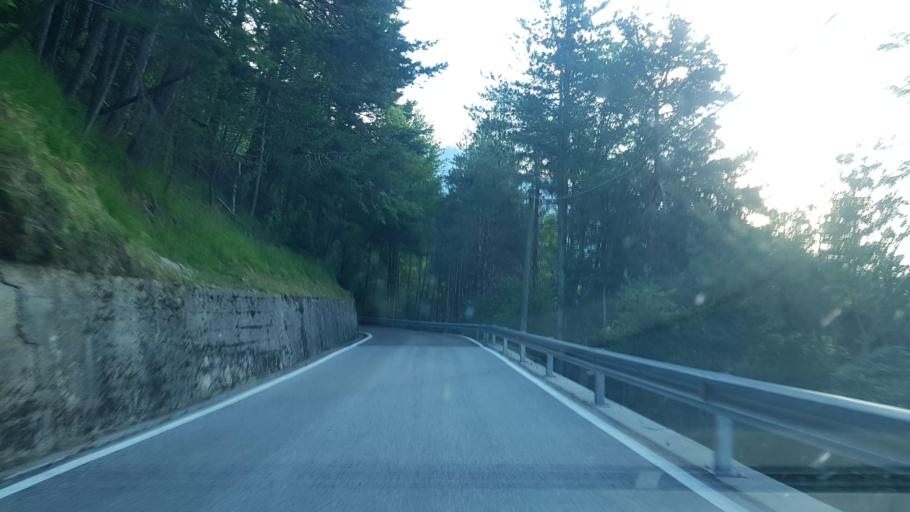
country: IT
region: Friuli Venezia Giulia
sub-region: Provincia di Udine
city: Dogna
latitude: 46.4512
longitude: 13.3707
